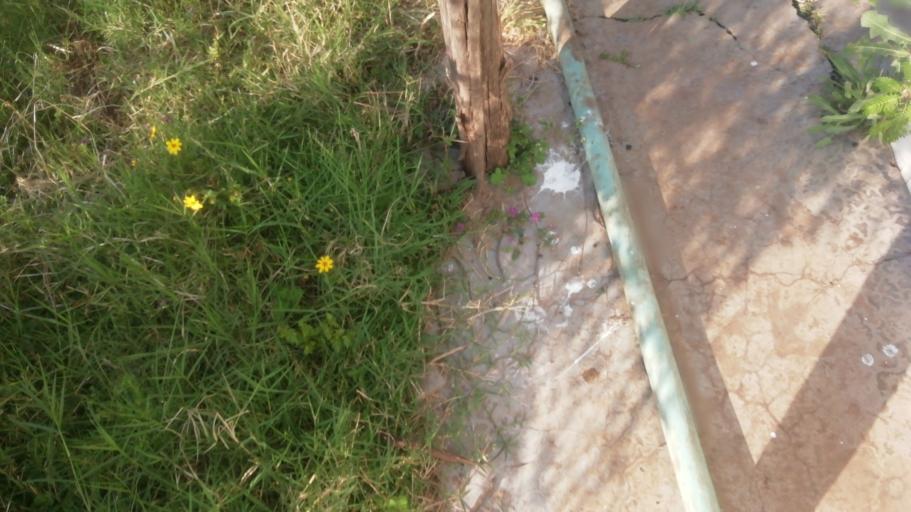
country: ET
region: Amhara
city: Addiet Canna
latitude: 11.2684
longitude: 37.8732
